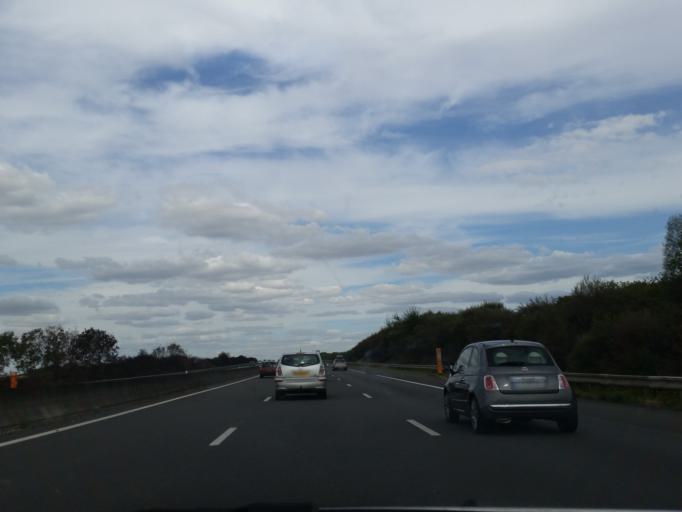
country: FR
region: Centre
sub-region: Departement d'Indre-et-Loire
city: Cangey
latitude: 47.5623
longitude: 1.0340
